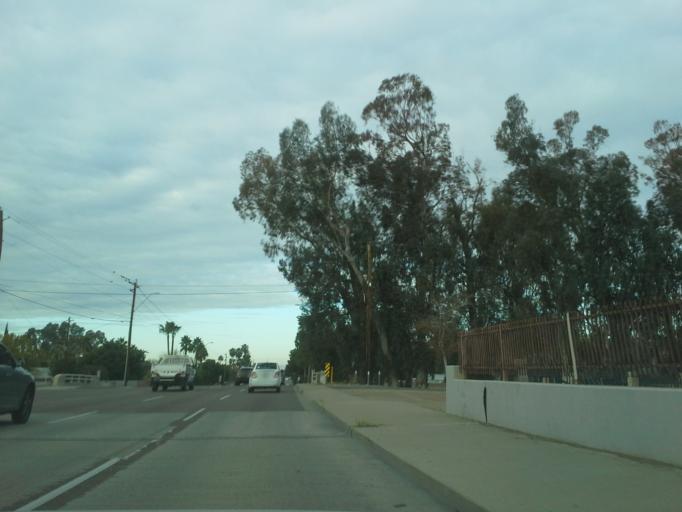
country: US
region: Arizona
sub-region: Maricopa County
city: Phoenix
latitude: 33.5528
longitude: -112.0612
